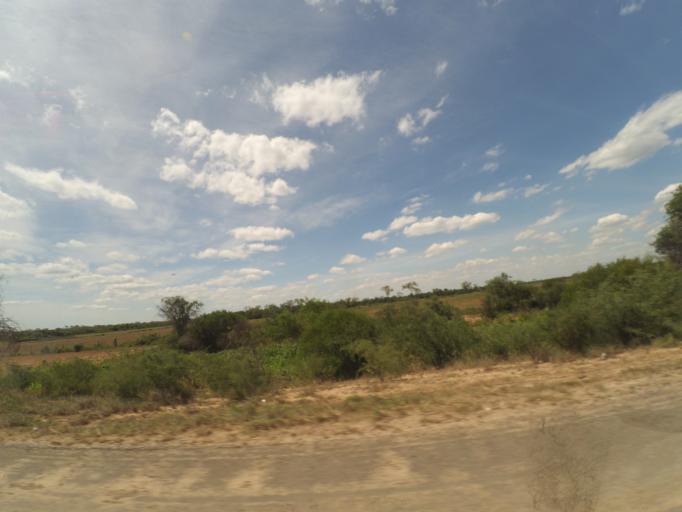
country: BO
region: Santa Cruz
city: Pailon
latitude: -17.5887
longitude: -61.9593
